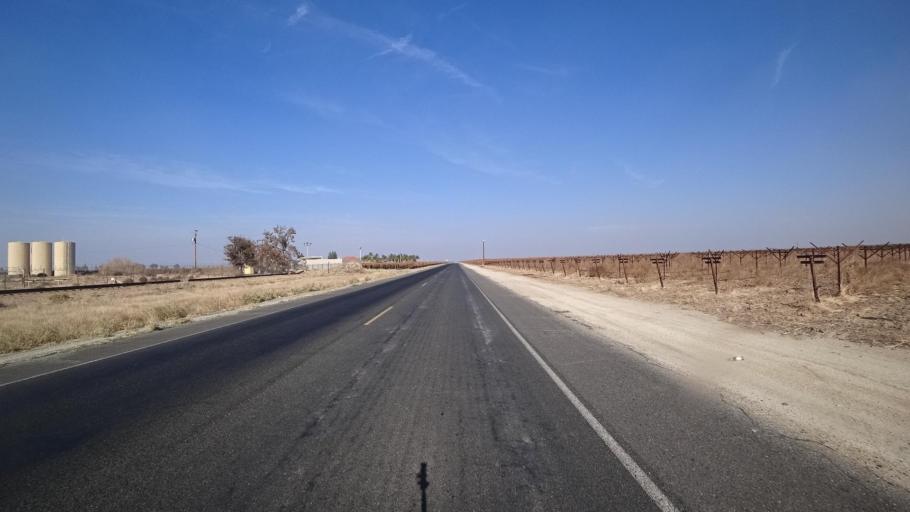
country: US
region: California
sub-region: Kern County
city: McFarland
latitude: 35.6772
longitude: -119.1848
